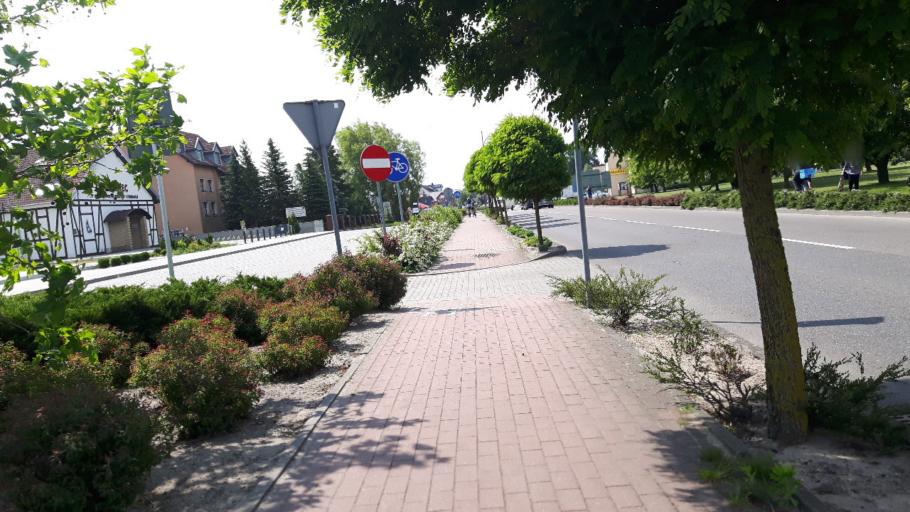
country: PL
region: Pomeranian Voivodeship
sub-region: Powiat leborski
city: Leba
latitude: 54.7558
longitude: 17.5629
